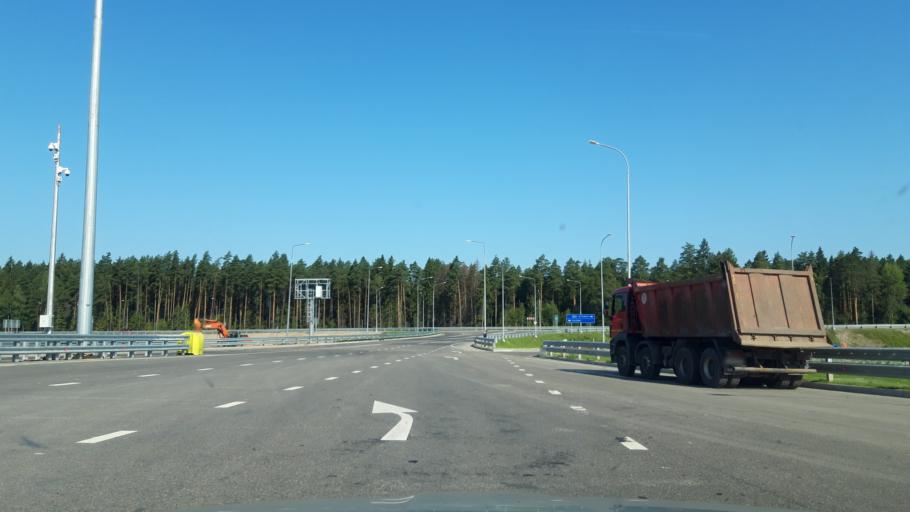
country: RU
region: Tverskaya
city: Novozavidovskiy
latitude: 56.5721
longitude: 36.4682
